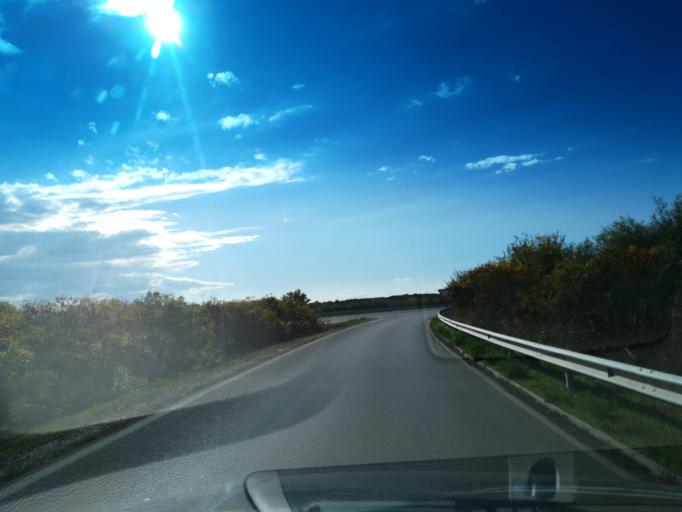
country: BG
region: Stara Zagora
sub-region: Obshtina Stara Zagora
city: Stara Zagora
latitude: 42.3388
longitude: 25.6586
